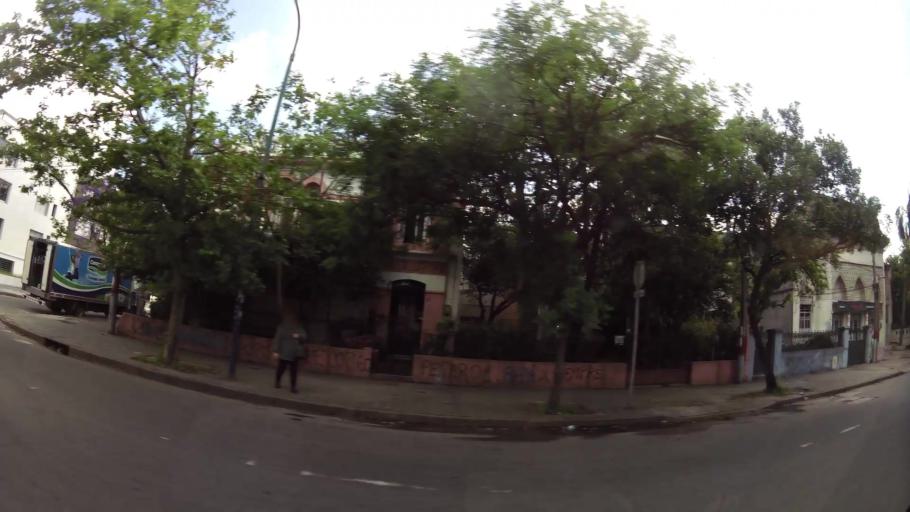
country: UY
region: Montevideo
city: Montevideo
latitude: -34.8632
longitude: -56.2110
